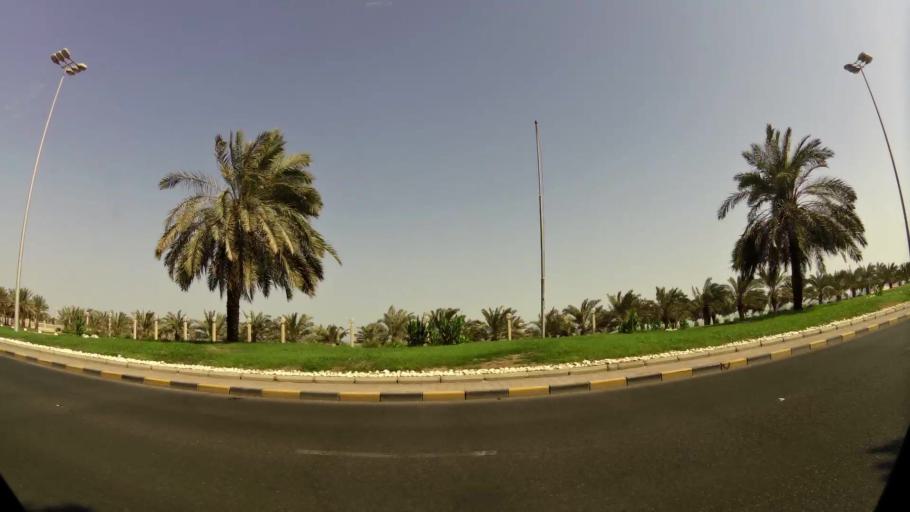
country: KW
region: Muhafazat Hawalli
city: Hawalli
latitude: 29.3572
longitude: 48.0265
